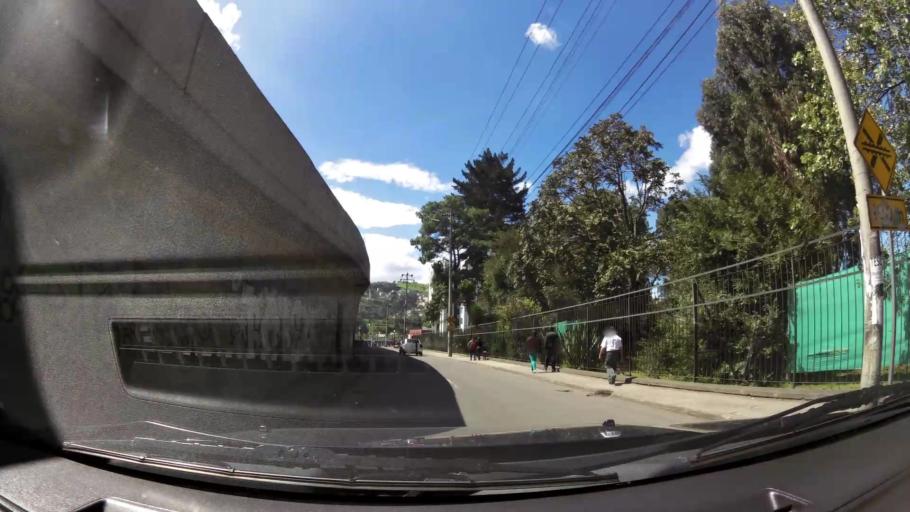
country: EC
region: Pichincha
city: Quito
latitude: -0.2889
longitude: -78.5398
